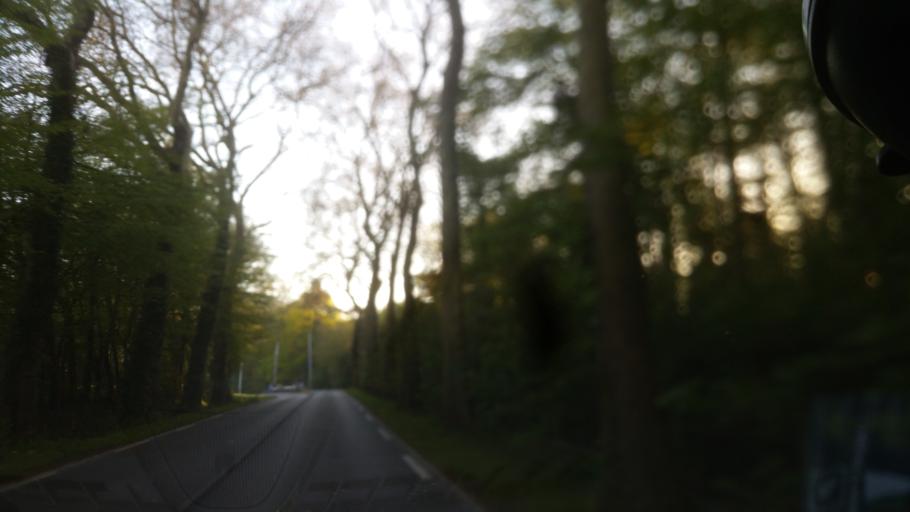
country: FR
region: Ile-de-France
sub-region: Departement de l'Essonne
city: Angervilliers
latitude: 48.5902
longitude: 2.0615
